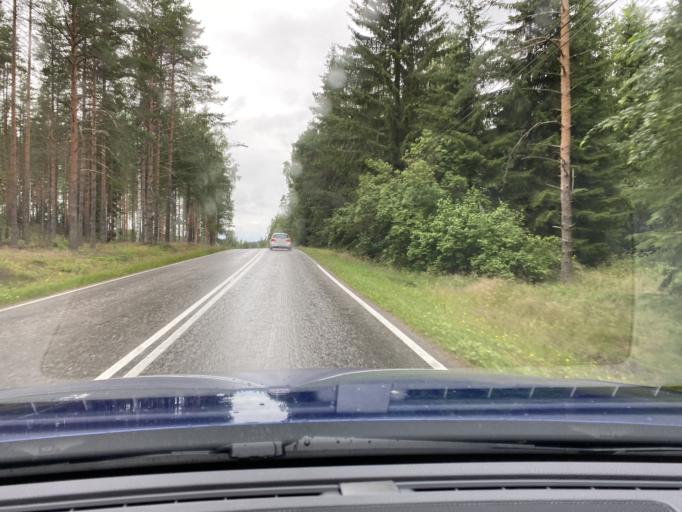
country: FI
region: Pirkanmaa
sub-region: Lounais-Pirkanmaa
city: Punkalaidun
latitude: 61.0605
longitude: 23.1842
